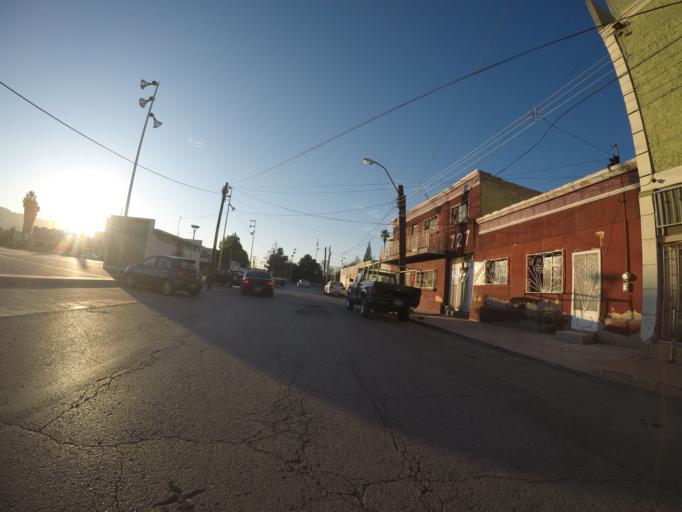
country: MX
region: Chihuahua
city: Ciudad Juarez
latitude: 31.7346
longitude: -106.4774
